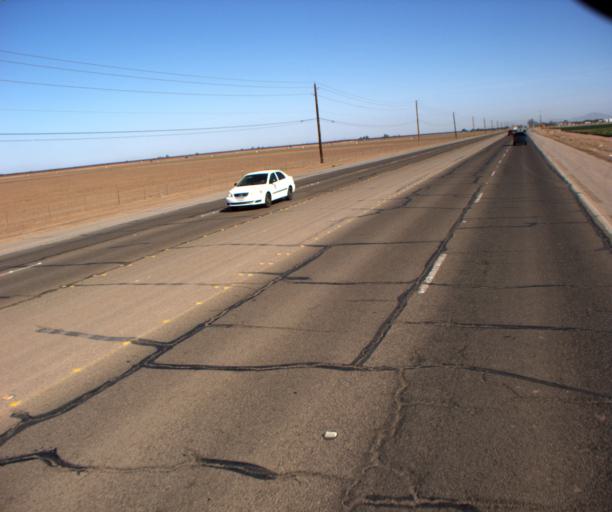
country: US
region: Arizona
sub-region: Yuma County
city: San Luis
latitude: 32.5316
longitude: -114.7867
